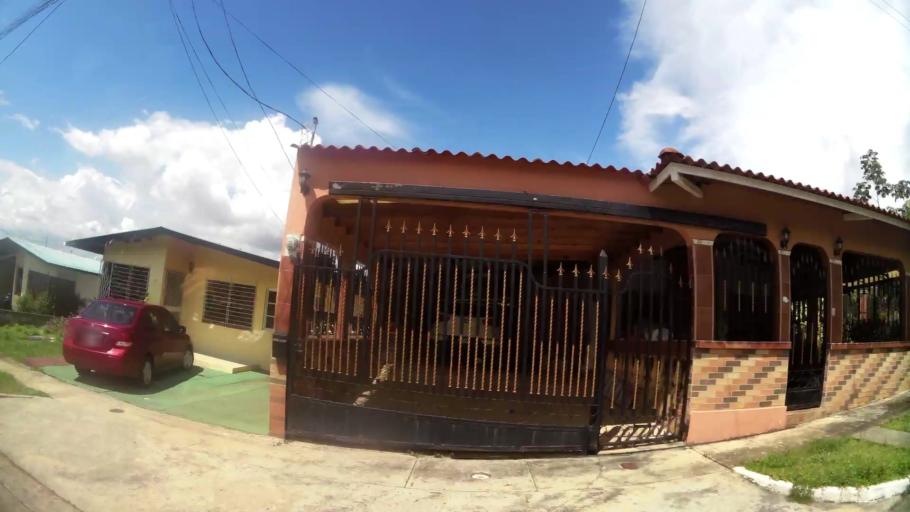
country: PA
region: Panama
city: San Vicente de Bique
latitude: 8.9207
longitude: -79.6908
